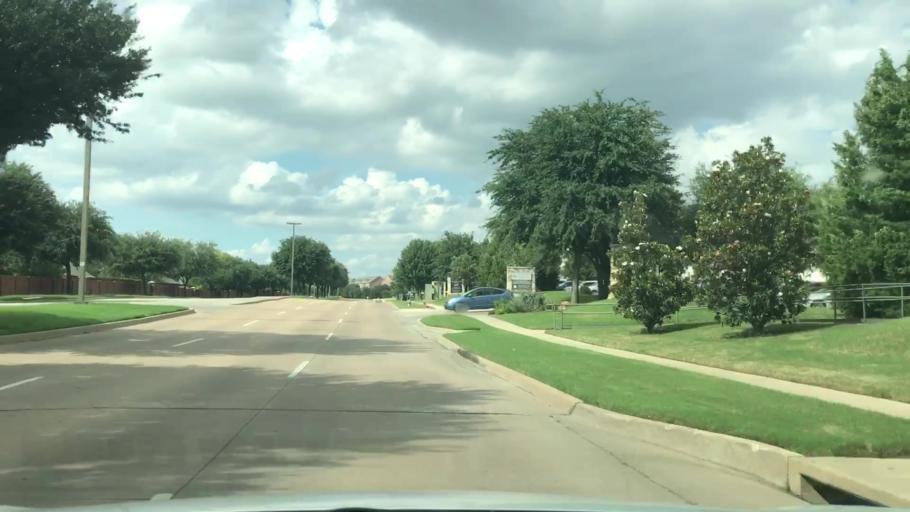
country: US
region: Texas
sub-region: Dallas County
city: Coppell
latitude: 32.9090
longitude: -96.9633
